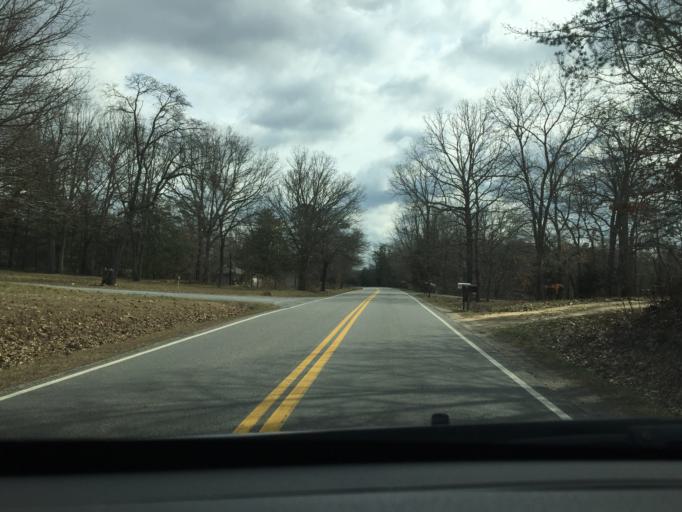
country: US
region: Virginia
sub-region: Campbell County
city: Rustburg
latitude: 37.3272
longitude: -79.1442
